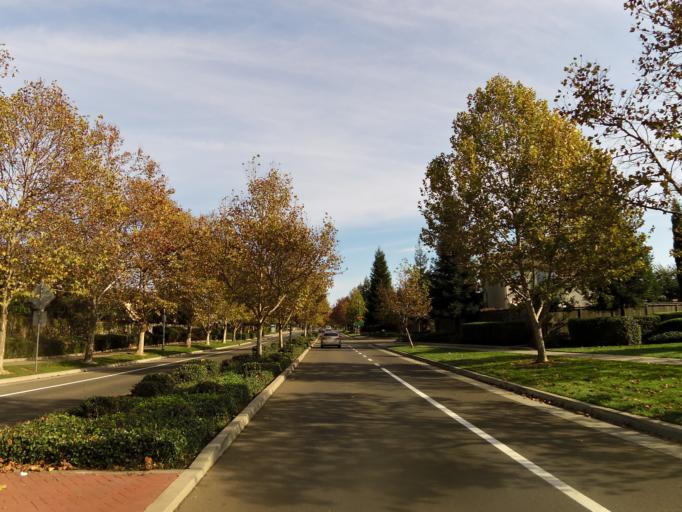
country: US
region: California
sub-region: Sacramento County
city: Elk Grove
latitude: 38.4091
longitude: -121.3478
